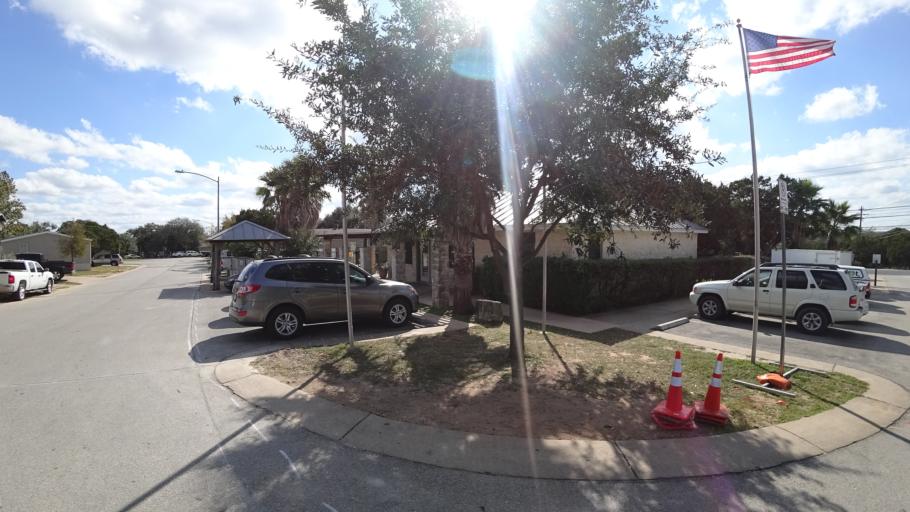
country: US
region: Texas
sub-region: Travis County
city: Barton Creek
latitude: 30.2501
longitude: -97.8861
